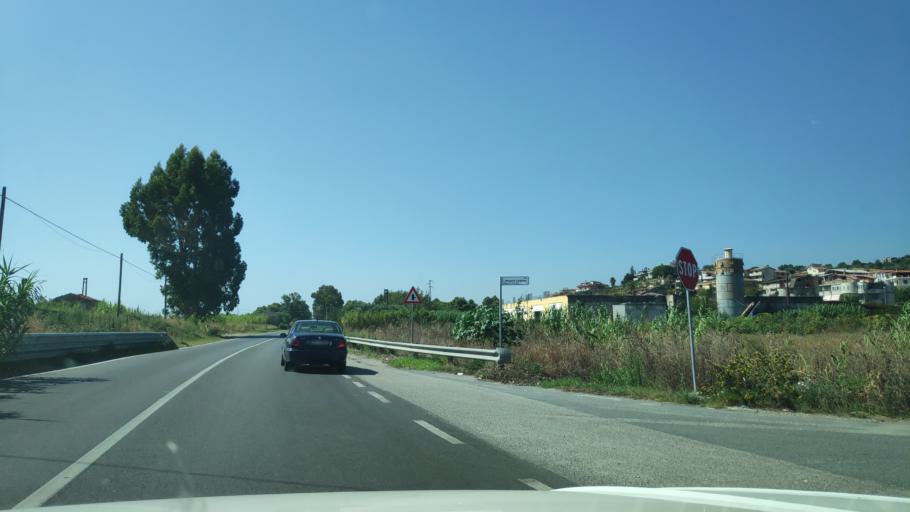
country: IT
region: Calabria
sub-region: Provincia di Reggio Calabria
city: Bovalino
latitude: 38.1248
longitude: 16.1595
